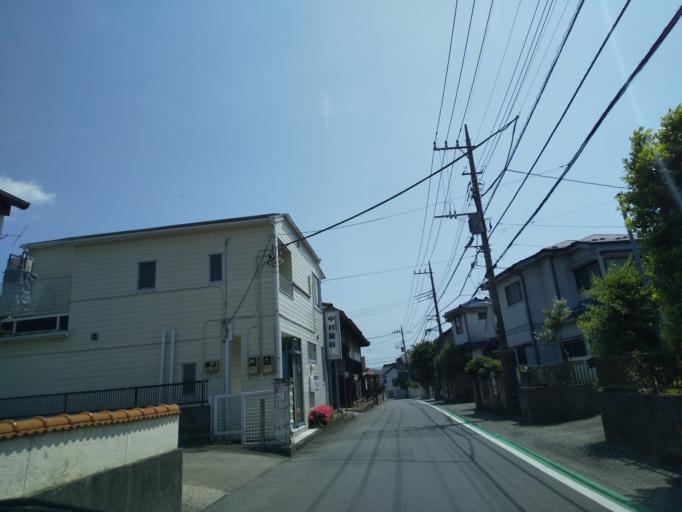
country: JP
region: Kanagawa
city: Zama
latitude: 35.5075
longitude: 139.3905
